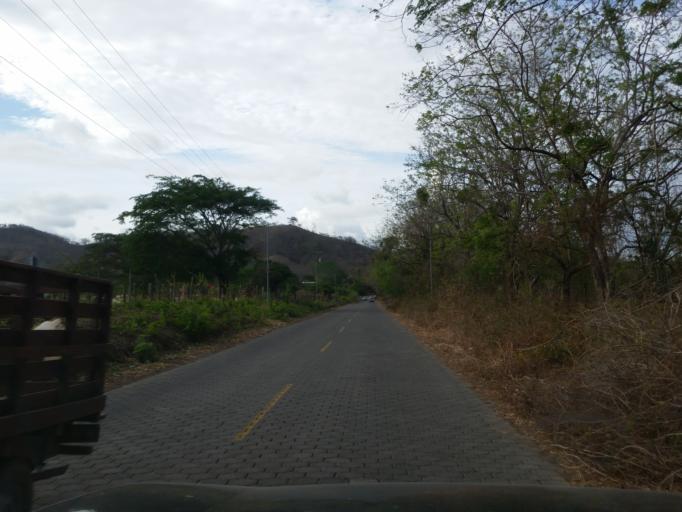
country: NI
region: Rivas
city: Tola
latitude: 11.4050
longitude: -85.9559
